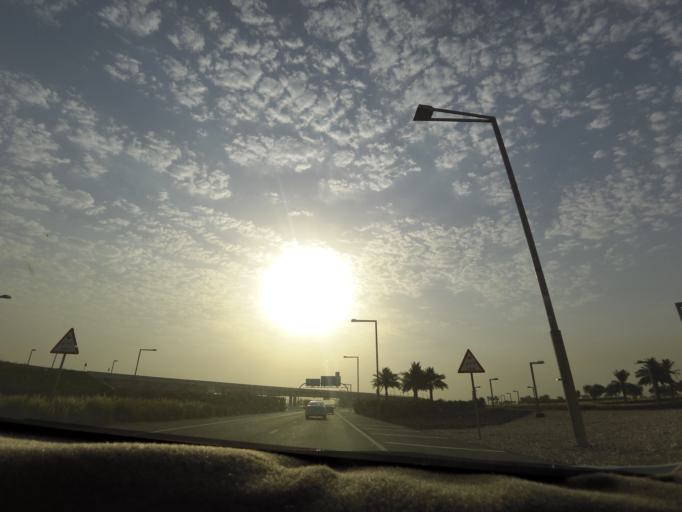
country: QA
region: Al Wakrah
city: Al Wakrah
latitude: 25.2466
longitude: 51.6051
